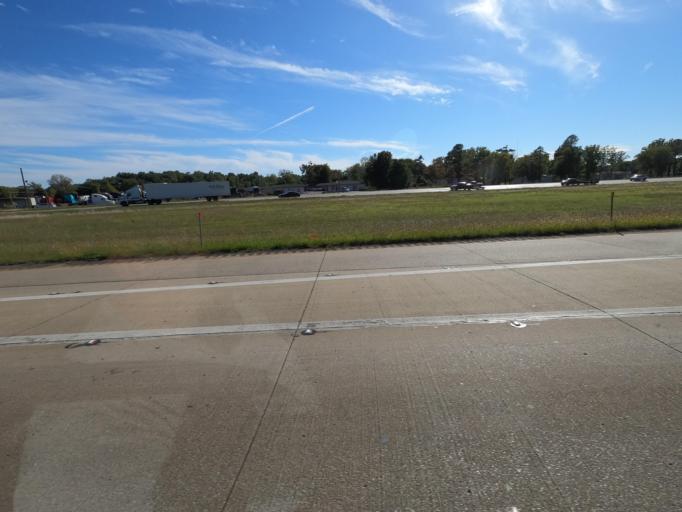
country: US
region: Arkansas
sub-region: Crittenden County
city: West Memphis
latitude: 35.1473
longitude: -90.1282
